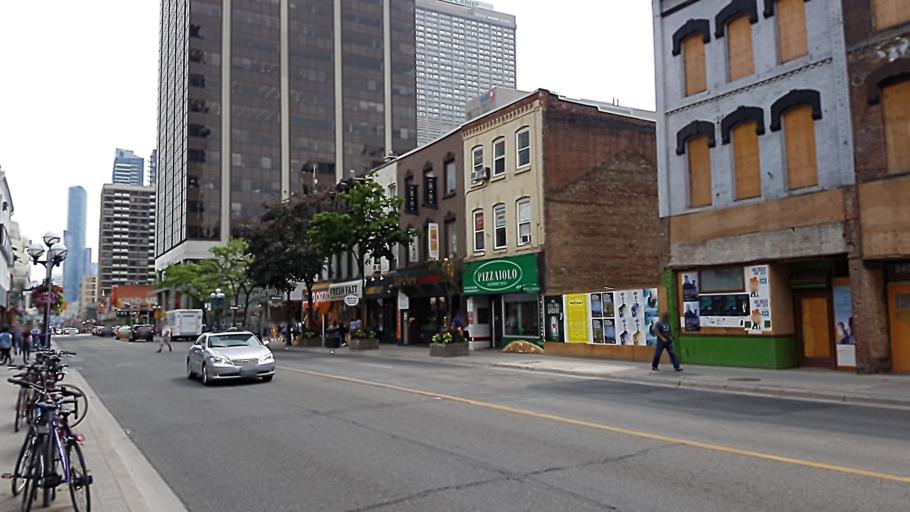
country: CA
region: Ontario
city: Toronto
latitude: 43.6716
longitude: -79.3877
